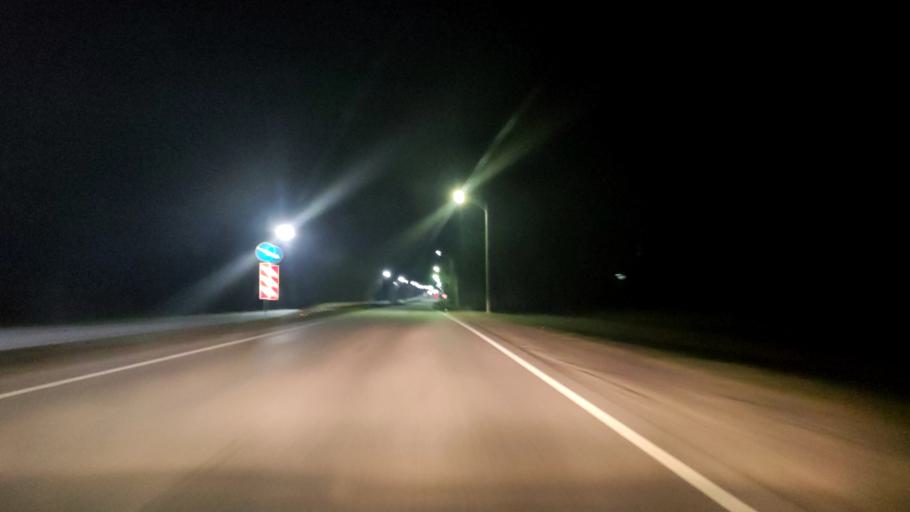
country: RU
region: Belgorod
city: Staryy Oskol
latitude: 51.4065
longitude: 37.8804
